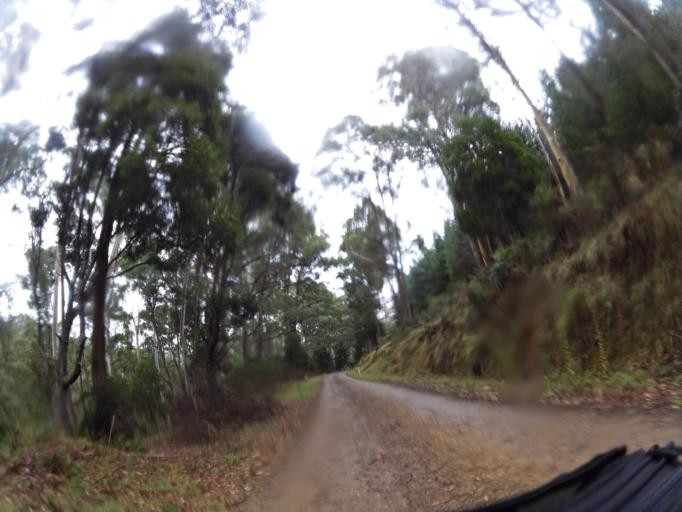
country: AU
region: New South Wales
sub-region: Greater Hume Shire
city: Holbrook
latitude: -36.1988
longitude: 147.5272
